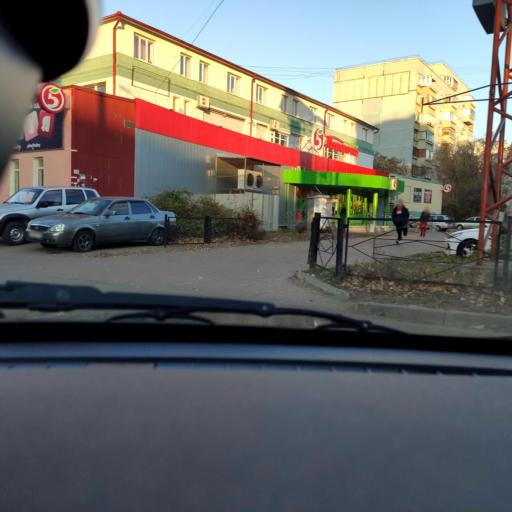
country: RU
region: Samara
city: Tol'yatti
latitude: 53.5464
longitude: 49.3390
